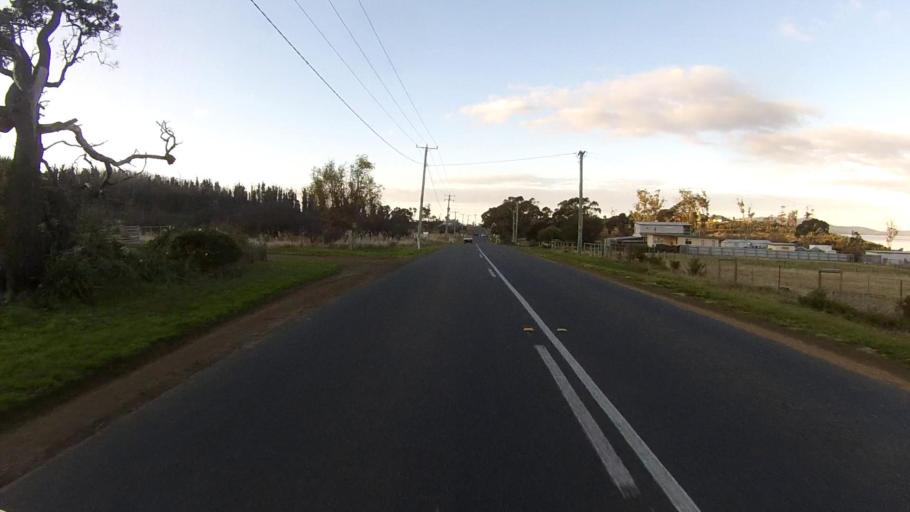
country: AU
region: Tasmania
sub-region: Sorell
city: Sorell
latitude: -42.8809
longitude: 147.8187
